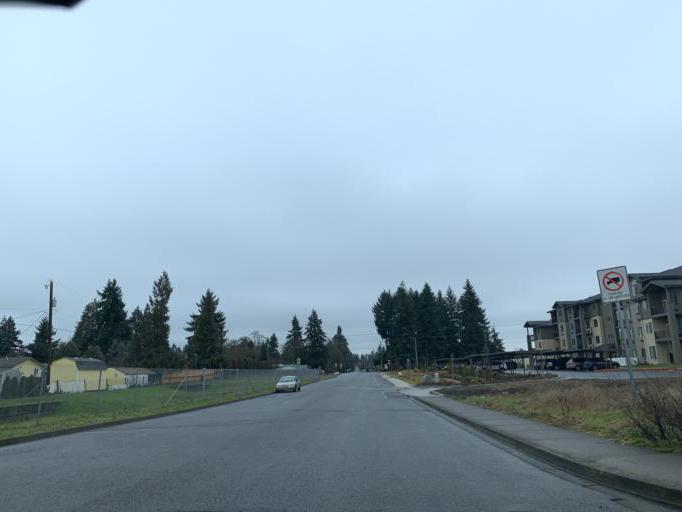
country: US
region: Washington
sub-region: Clark County
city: Five Corners
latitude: 45.6844
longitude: -122.5782
